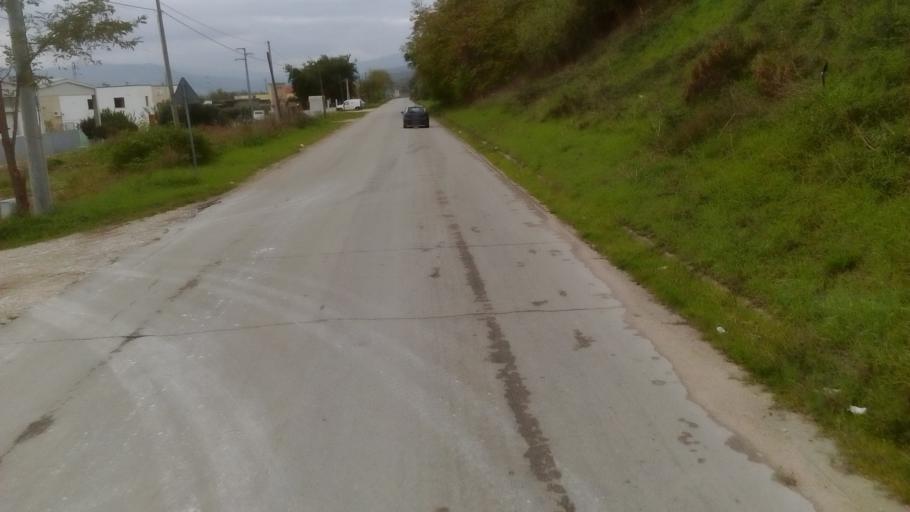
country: IT
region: Abruzzo
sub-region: Provincia di Chieti
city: San Salvo
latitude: 42.0310
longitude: 14.7414
